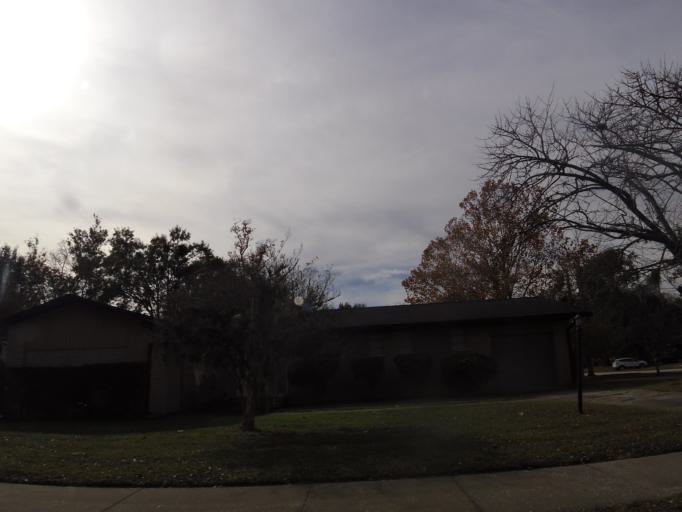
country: US
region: Florida
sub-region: Duval County
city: Jacksonville
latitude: 30.2262
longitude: -81.5948
